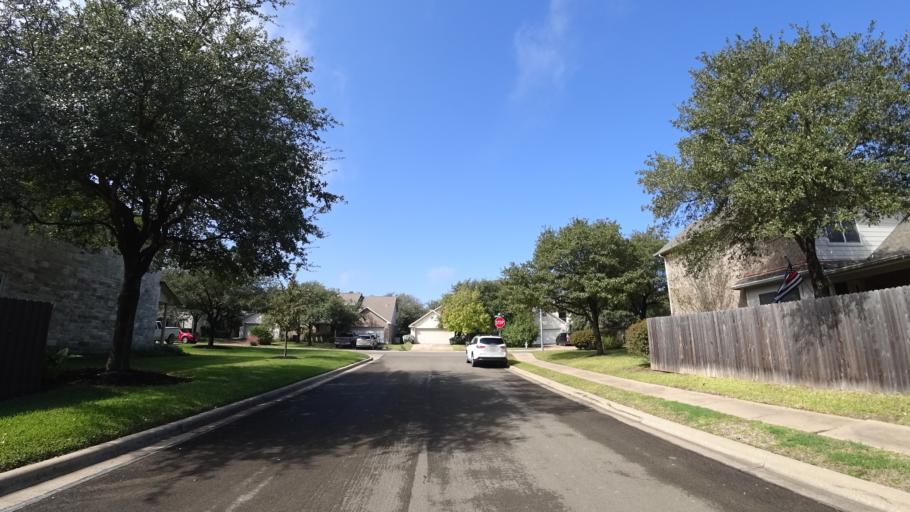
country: US
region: Texas
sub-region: Travis County
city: Shady Hollow
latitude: 30.2061
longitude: -97.8770
